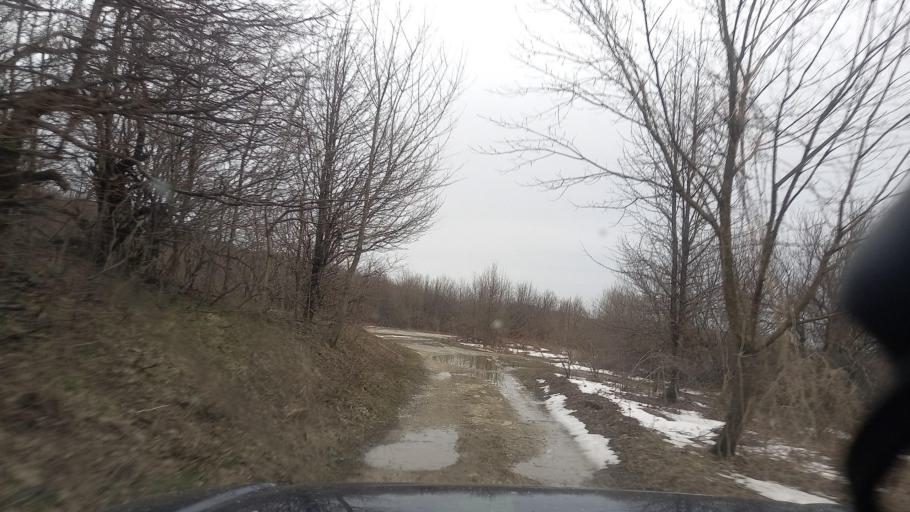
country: RU
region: Krasnodarskiy
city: Pshada
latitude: 44.5954
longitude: 38.3195
